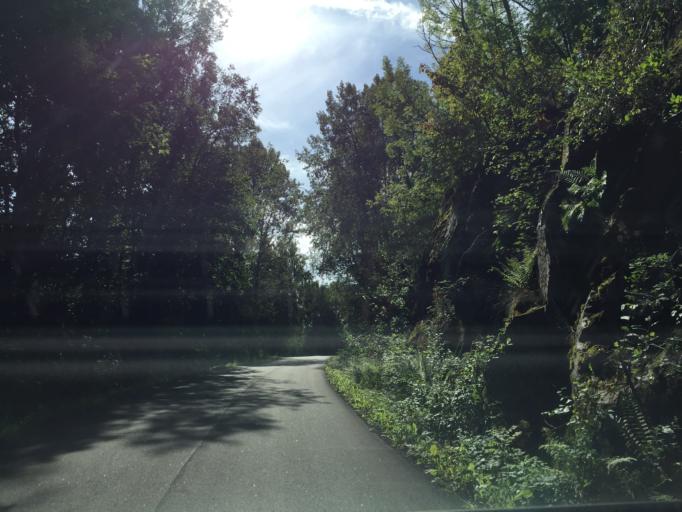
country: NO
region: Vestfold
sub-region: Hof
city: Hof
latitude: 59.4656
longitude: 10.1466
